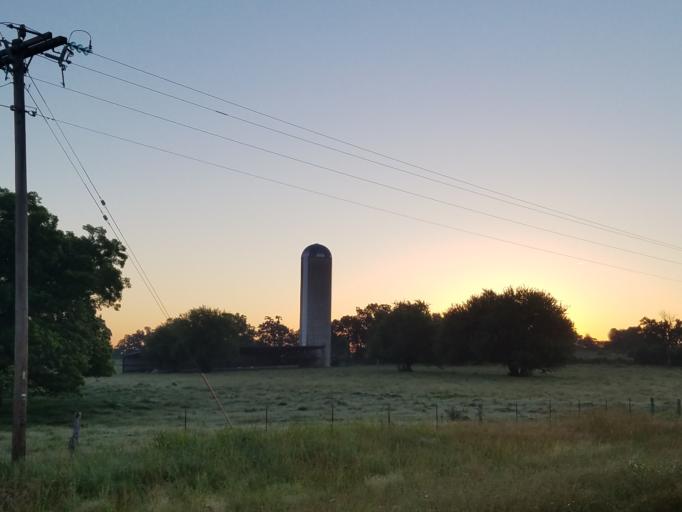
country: US
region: Oklahoma
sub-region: Coal County
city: Coalgate
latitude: 34.5055
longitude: -96.3754
